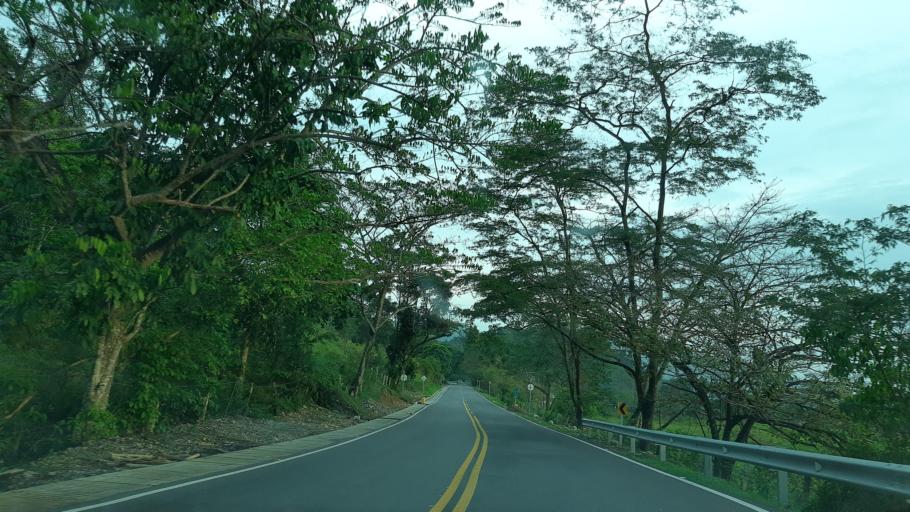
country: CO
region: Casanare
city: Sabanalarga
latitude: 4.7791
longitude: -73.0503
